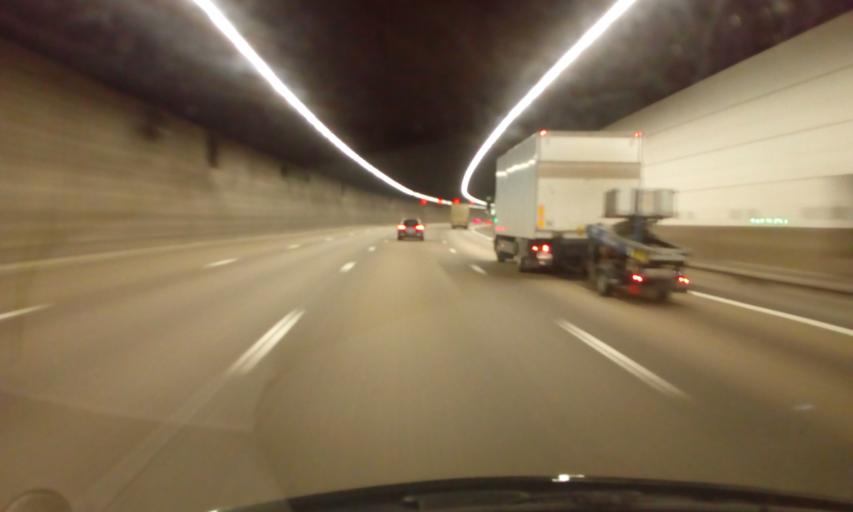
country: BE
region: Flanders
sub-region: Provincie Antwerpen
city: Mortsel
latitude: 51.1828
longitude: 4.4175
